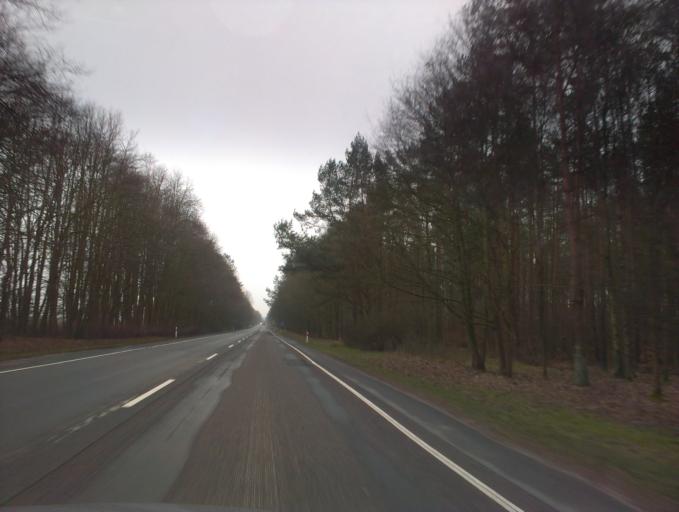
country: PL
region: Greater Poland Voivodeship
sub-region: Powiat pilski
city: Ujscie
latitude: 53.0268
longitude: 16.8001
